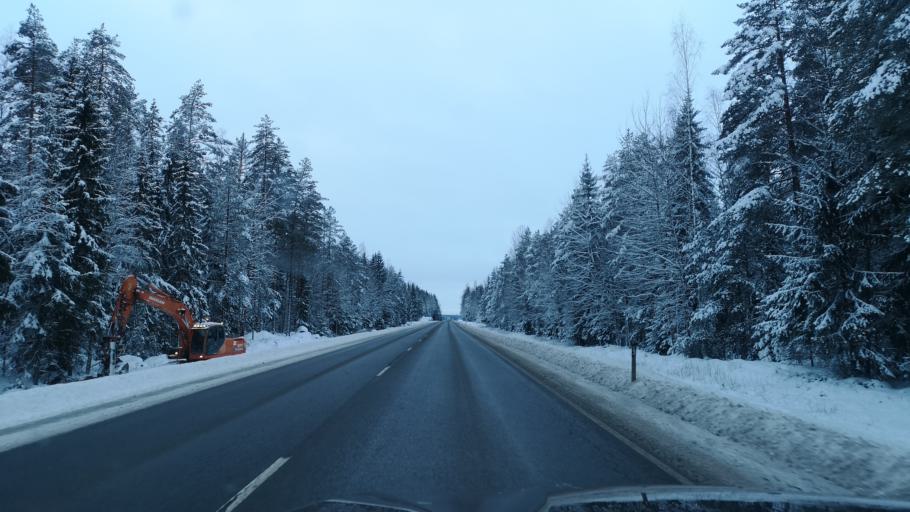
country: FI
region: Varsinais-Suomi
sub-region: Loimaa
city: Loimaa
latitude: 60.9020
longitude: 23.1418
